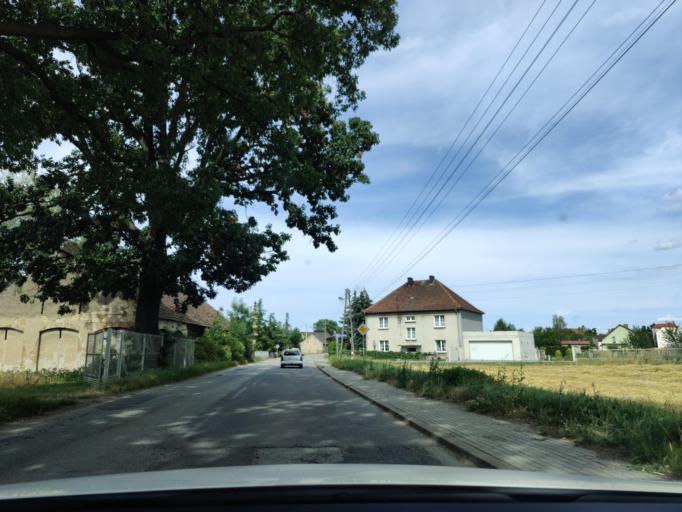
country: PL
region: Opole Voivodeship
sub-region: Powiat krapkowicki
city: Strzeleczki
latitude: 50.4561
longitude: 17.8496
